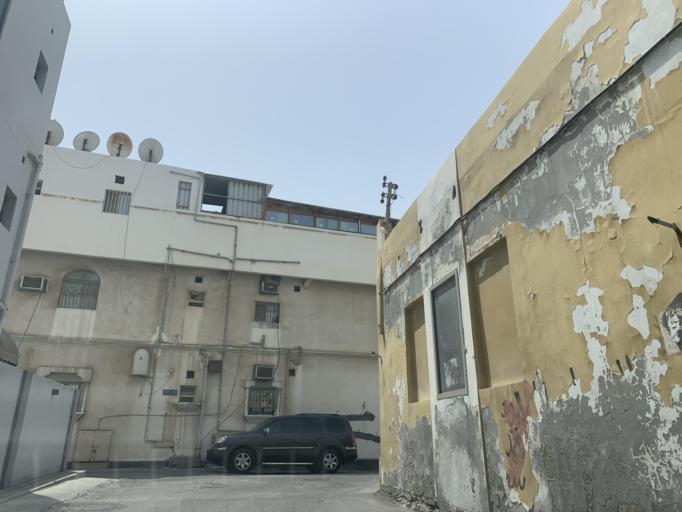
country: BH
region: Northern
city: Madinat `Isa
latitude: 26.1816
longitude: 50.5529
